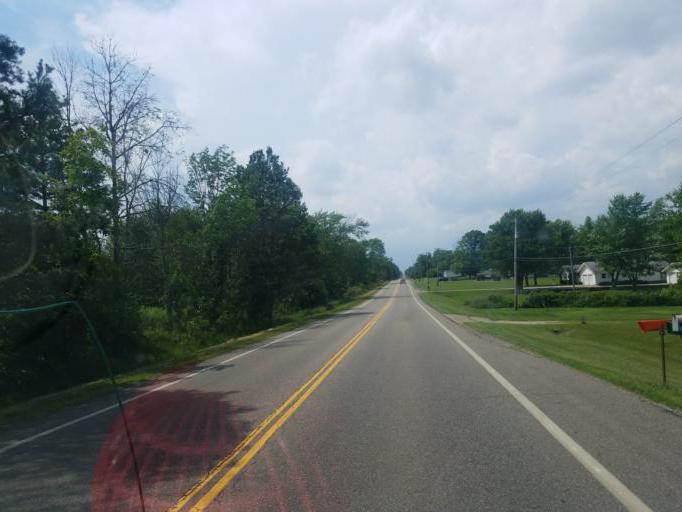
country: US
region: Ohio
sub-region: Portage County
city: Ravenna
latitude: 41.0847
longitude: -81.1280
